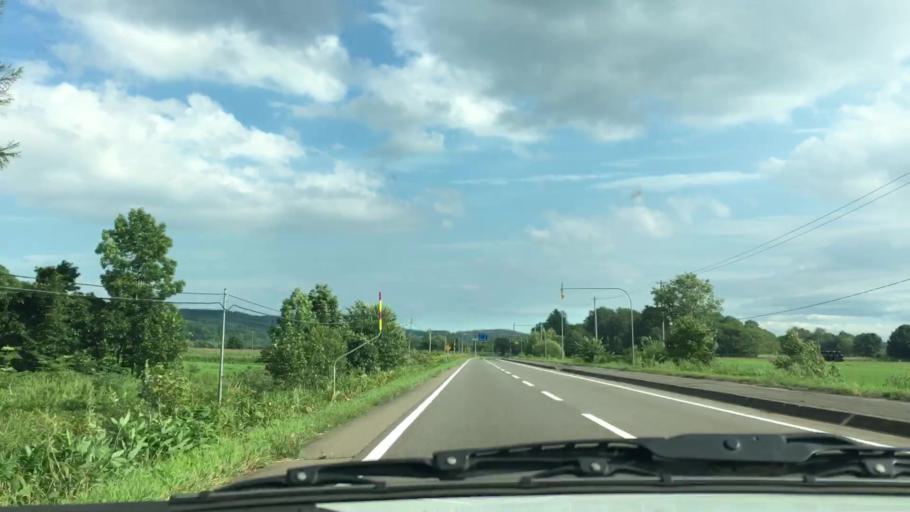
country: JP
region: Hokkaido
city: Otofuke
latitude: 43.3264
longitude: 143.2979
